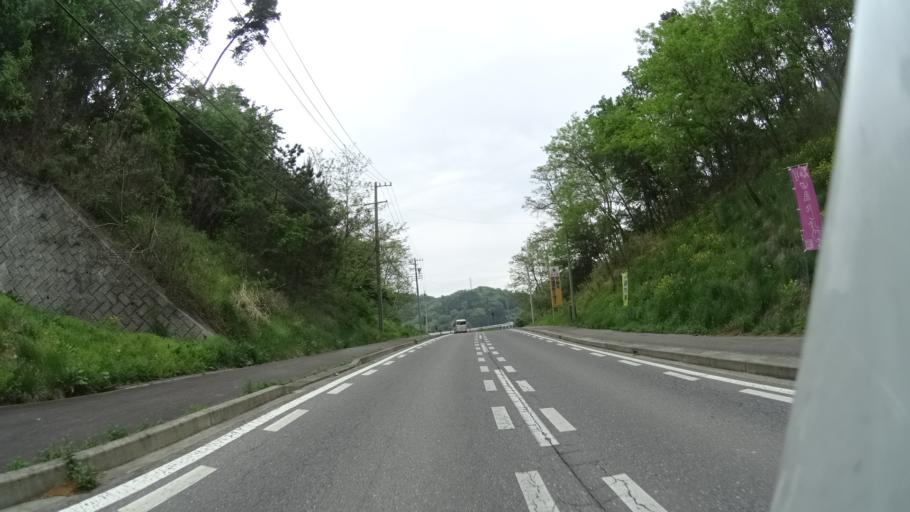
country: JP
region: Nagano
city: Kamimaruko
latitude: 36.3534
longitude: 138.1672
